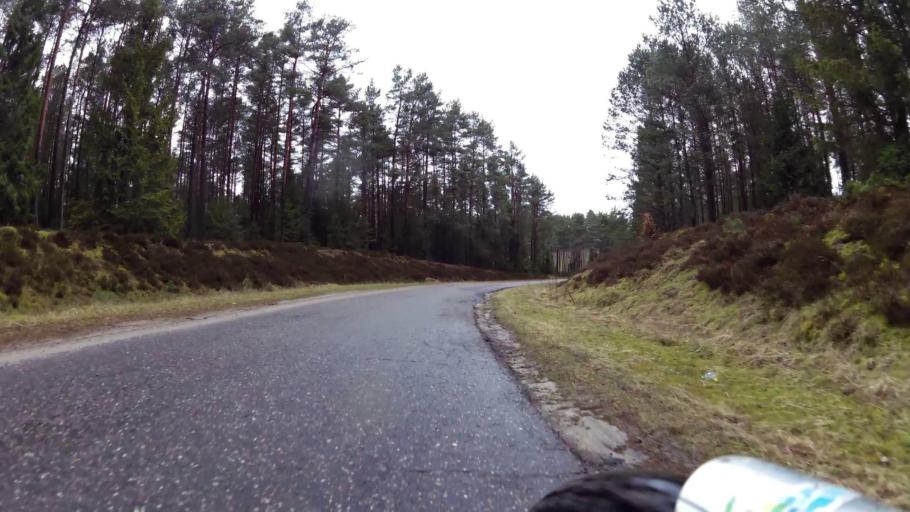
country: PL
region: Pomeranian Voivodeship
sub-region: Powiat bytowski
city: Borzytuchom
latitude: 54.2645
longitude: 17.3664
